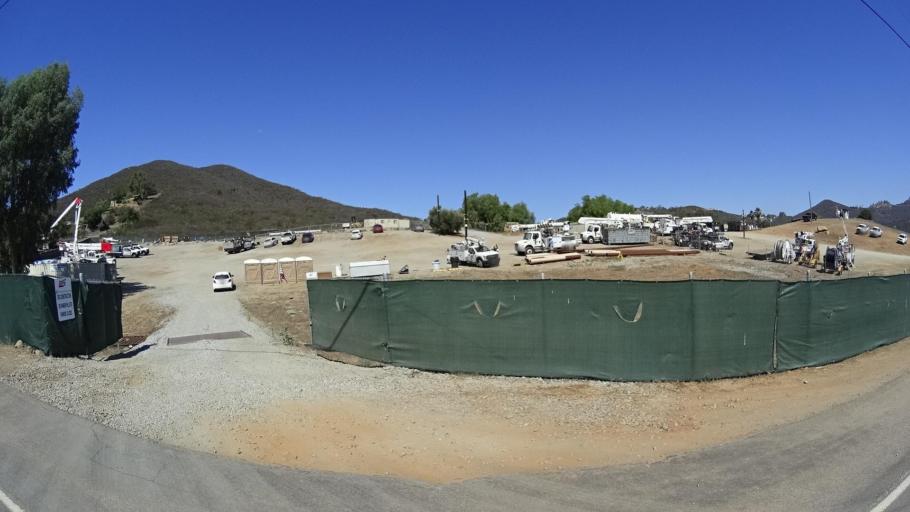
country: US
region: California
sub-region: San Diego County
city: Rainbow
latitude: 33.4013
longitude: -117.1700
